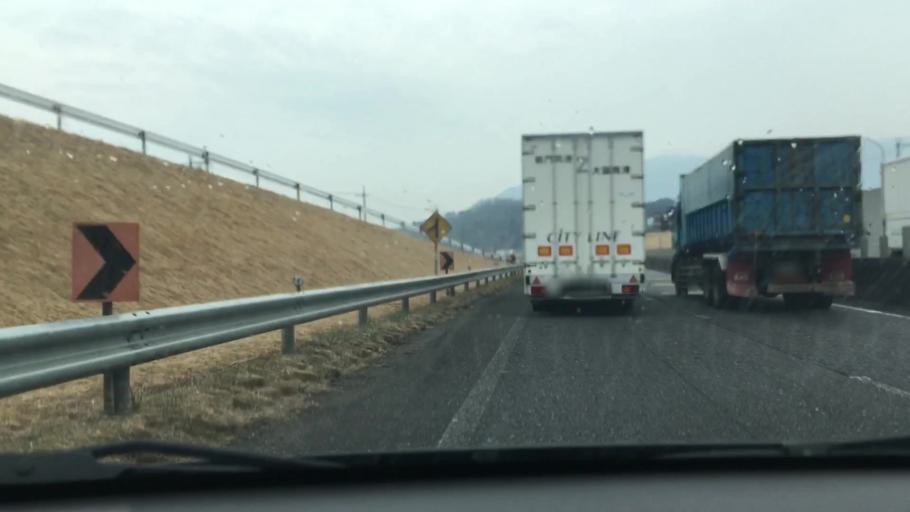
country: JP
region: Mie
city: Ueno-ebisumachi
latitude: 34.8123
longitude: 136.2046
